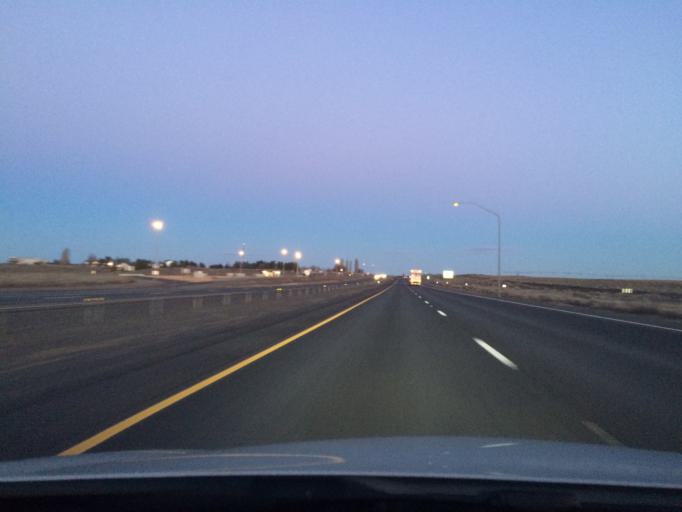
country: US
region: Washington
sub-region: Grant County
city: Royal City
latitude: 47.1037
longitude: -119.6195
